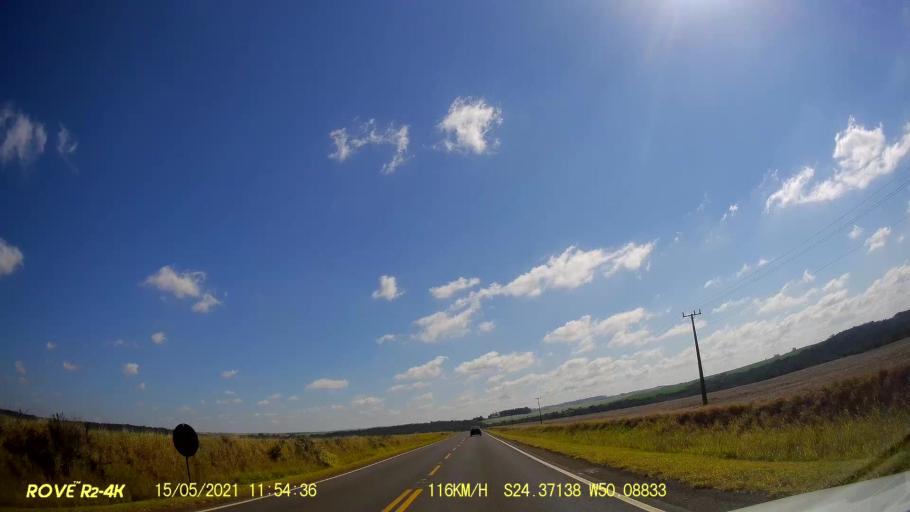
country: BR
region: Parana
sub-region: Pirai Do Sul
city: Pirai do Sul
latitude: -24.3712
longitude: -50.0885
